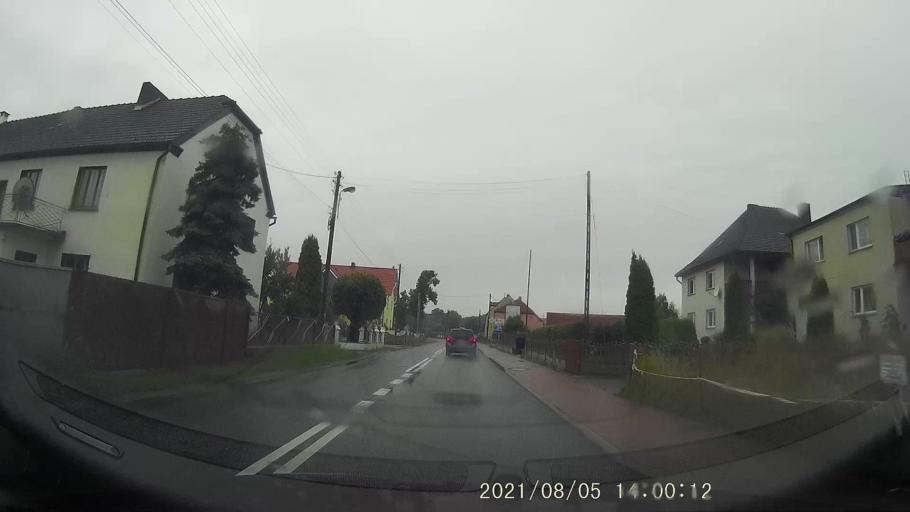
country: PL
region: Opole Voivodeship
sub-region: Powiat krapkowicki
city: Strzeleczki
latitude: 50.4506
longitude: 17.9030
